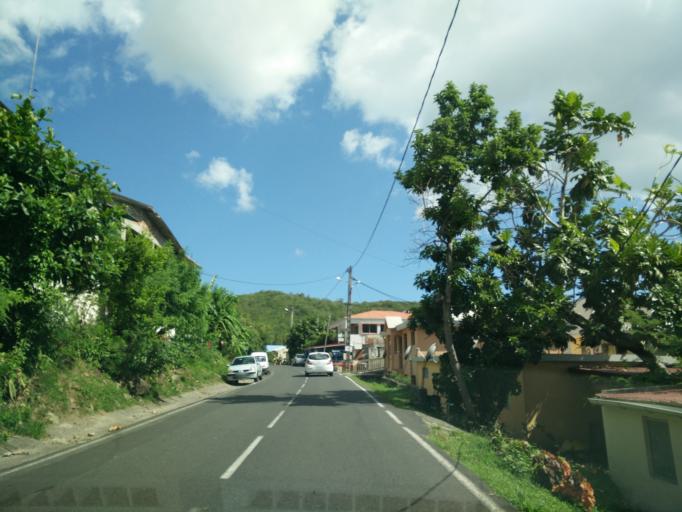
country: MQ
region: Martinique
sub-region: Martinique
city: Les Trois-Ilets
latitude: 14.5031
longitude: -61.0838
